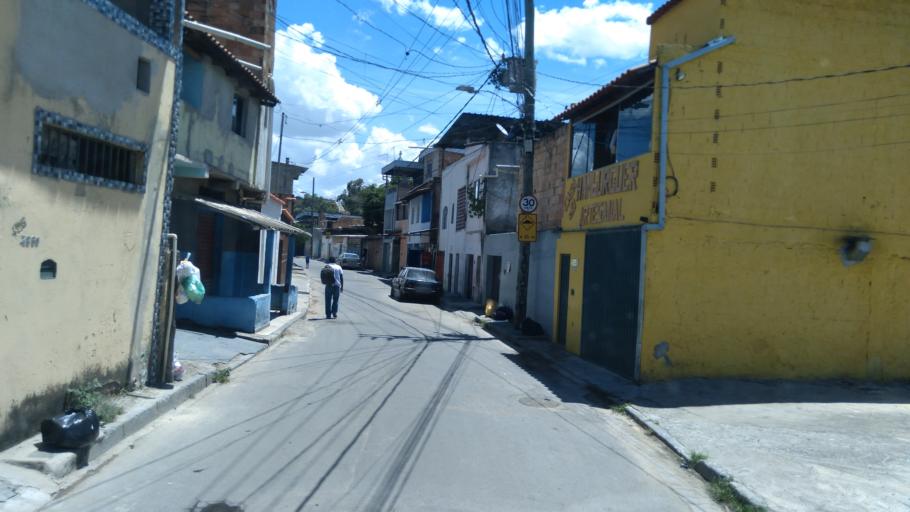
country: BR
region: Minas Gerais
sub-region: Santa Luzia
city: Santa Luzia
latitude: -19.8337
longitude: -43.8935
